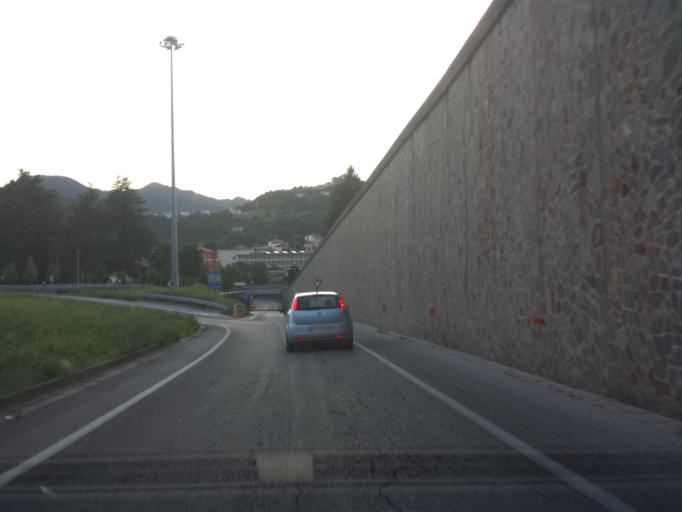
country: IT
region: Veneto
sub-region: Provincia di Vicenza
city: Valdagno
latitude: 45.6536
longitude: 11.3062
